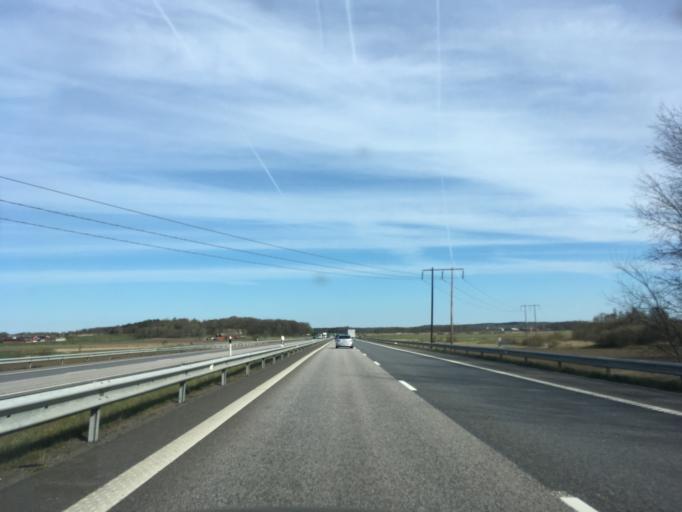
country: SE
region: Halland
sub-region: Varbergs Kommun
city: Traslovslage
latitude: 57.1014
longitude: 12.3376
